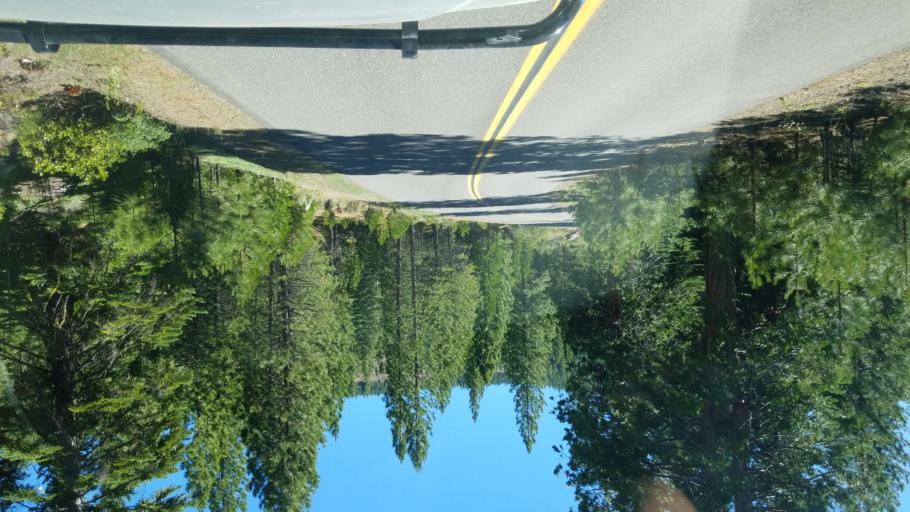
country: US
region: California
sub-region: Lassen County
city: Susanville
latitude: 40.5113
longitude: -120.7744
